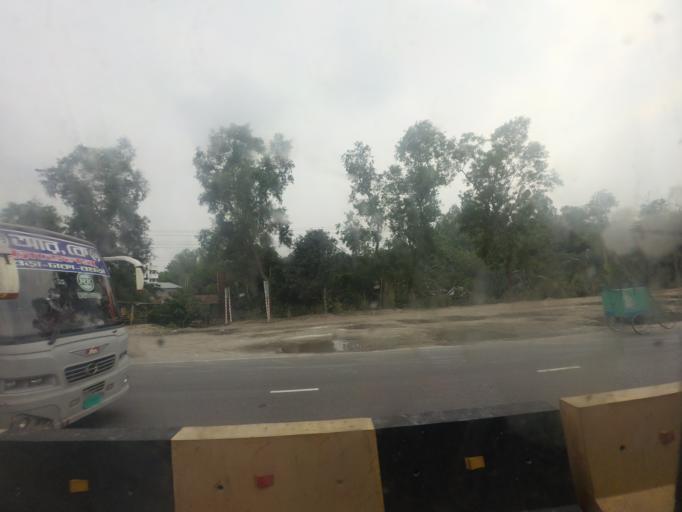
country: BD
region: Rajshahi
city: Sirajganj
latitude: 24.3924
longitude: 89.7137
